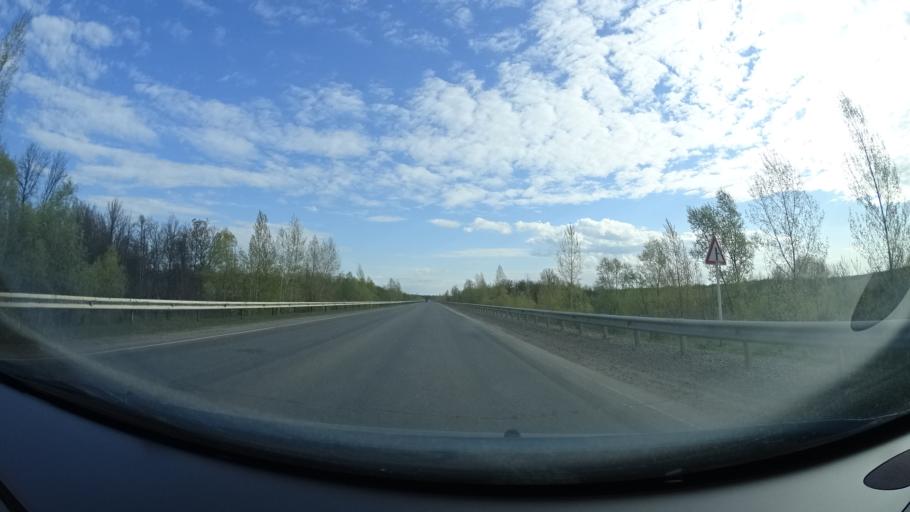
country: RU
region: Bashkortostan
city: Blagoveshchensk
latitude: 55.0348
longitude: 55.8028
